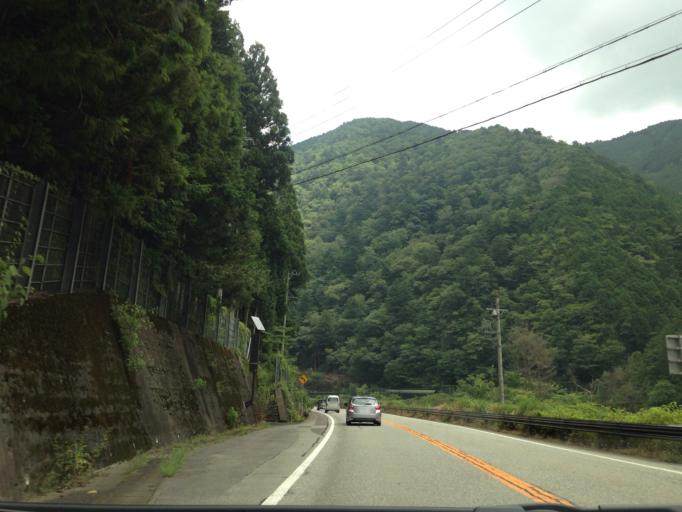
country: JP
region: Gifu
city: Gujo
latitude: 35.7537
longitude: 137.2275
